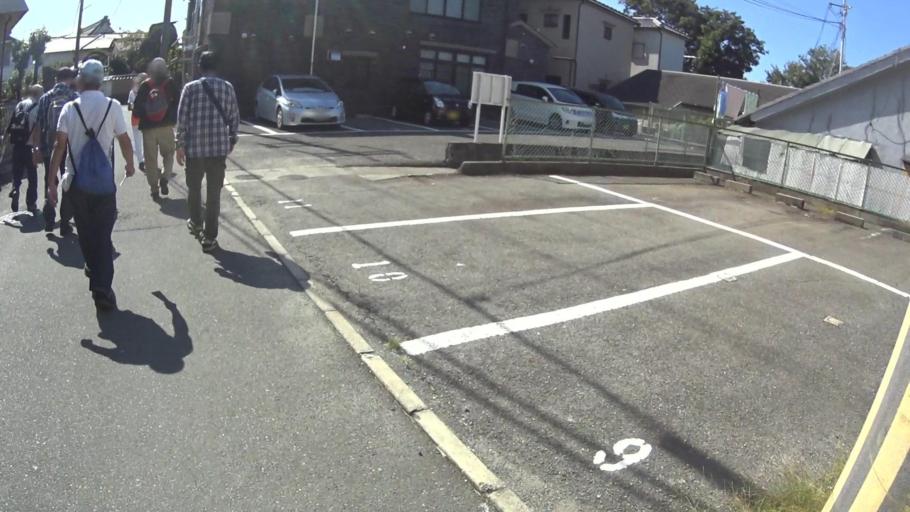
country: JP
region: Osaka
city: Takaishi
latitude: 34.5358
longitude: 135.4763
